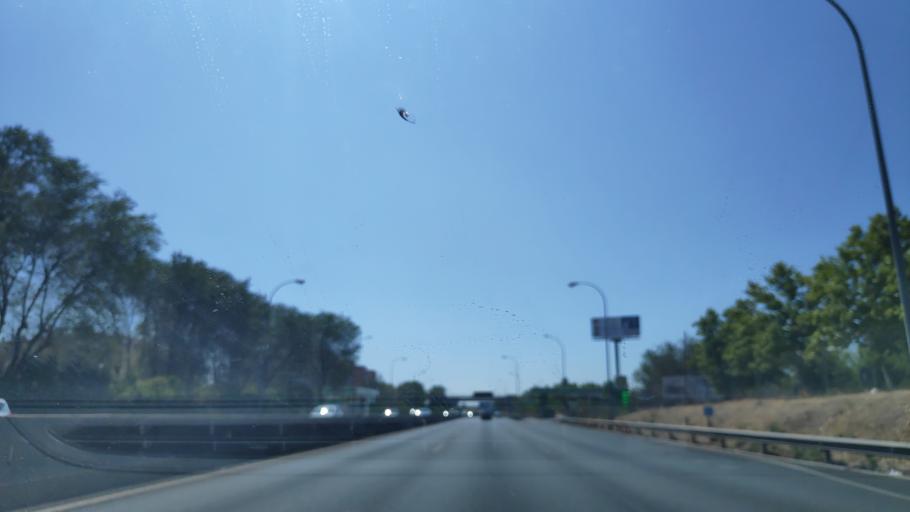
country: ES
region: Madrid
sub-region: Provincia de Madrid
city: Getafe
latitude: 40.3045
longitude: -3.7394
